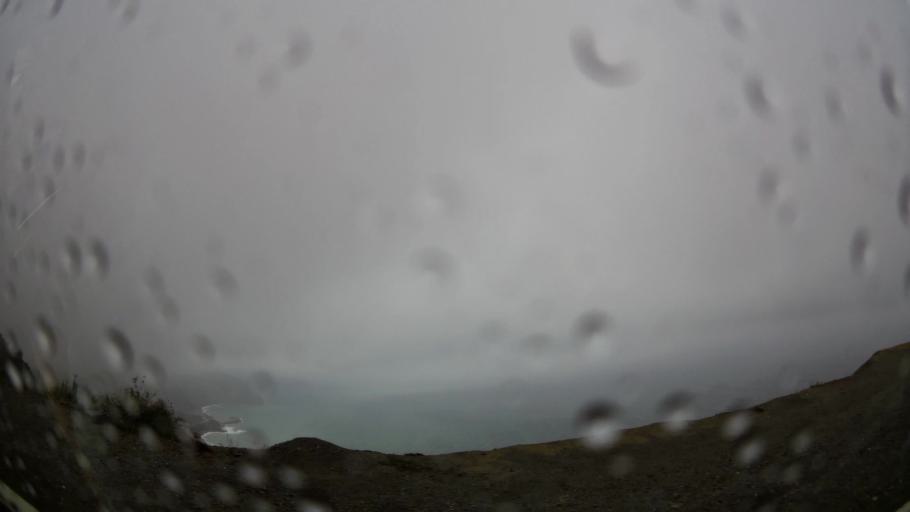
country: MA
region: Taza-Al Hoceima-Taounate
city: Tirhanimine
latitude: 35.2385
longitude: -3.9675
